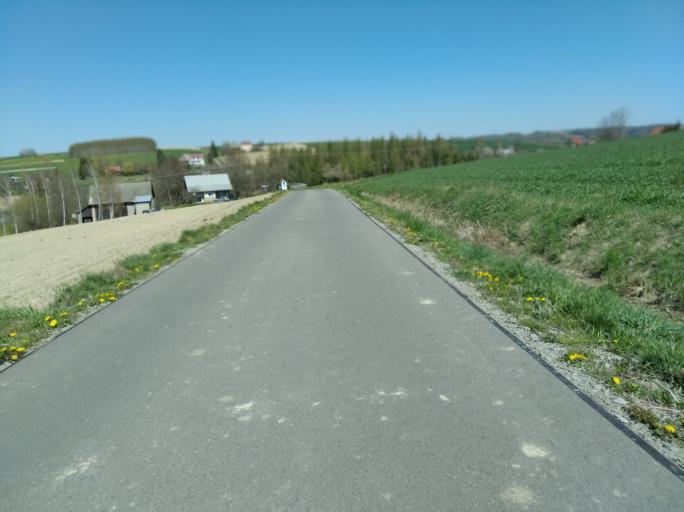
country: PL
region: Subcarpathian Voivodeship
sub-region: Powiat strzyzowski
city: Wisniowa
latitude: 49.9073
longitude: 21.6867
